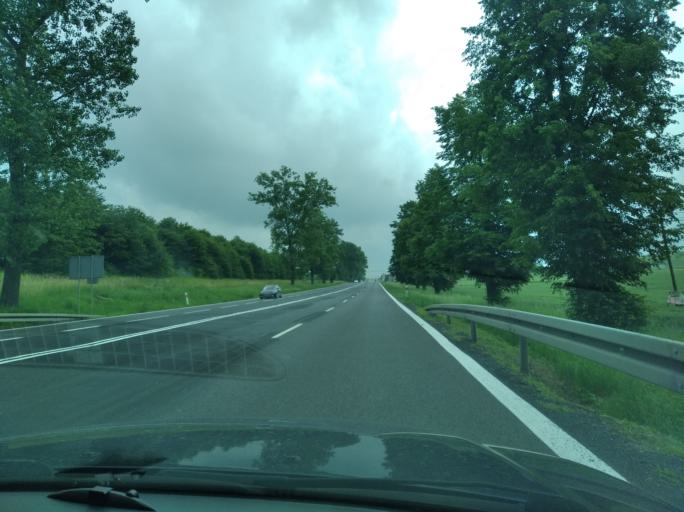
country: PL
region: Subcarpathian Voivodeship
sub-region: Powiat przeworski
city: Przeworsk
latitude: 50.0523
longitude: 22.5201
